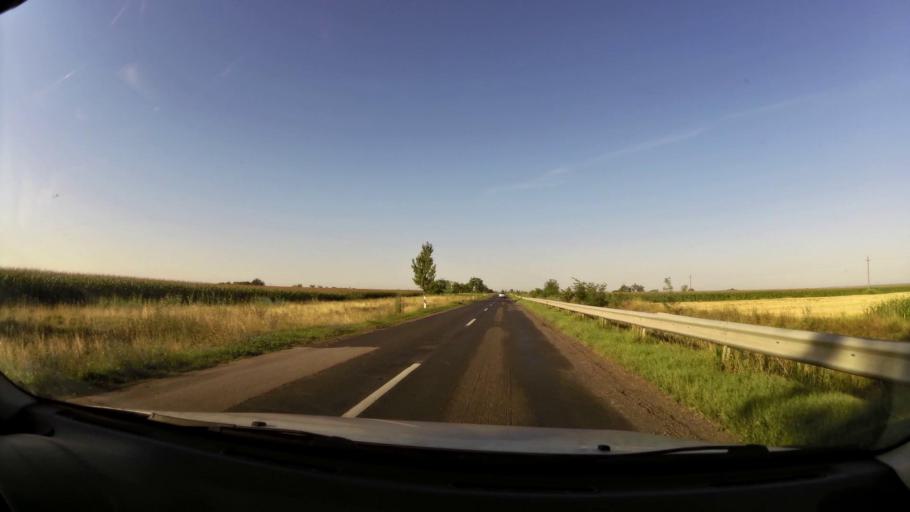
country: HU
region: Pest
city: Tapioszolos
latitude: 47.2662
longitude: 19.8598
